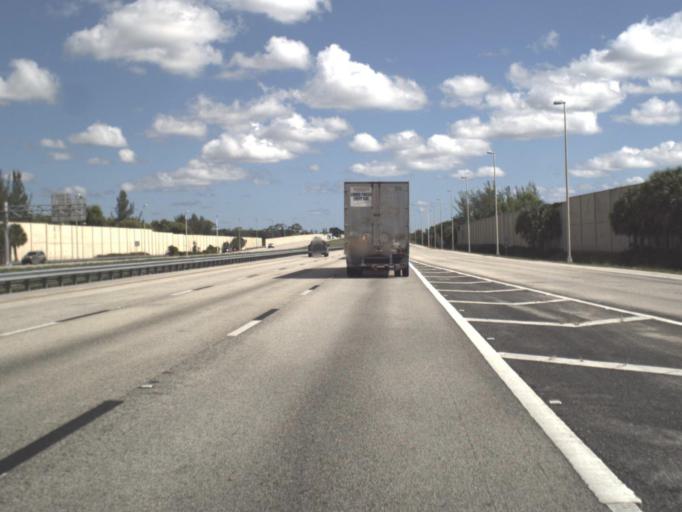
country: US
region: Florida
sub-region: Broward County
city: Parkland
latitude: 26.3016
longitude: -80.2448
